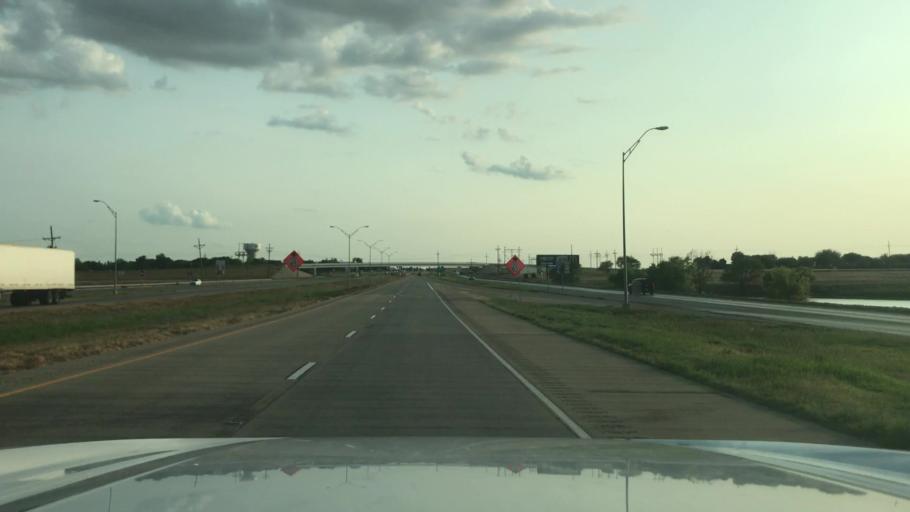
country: US
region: Texas
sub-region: Hale County
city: Plainview
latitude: 34.2081
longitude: -101.7382
